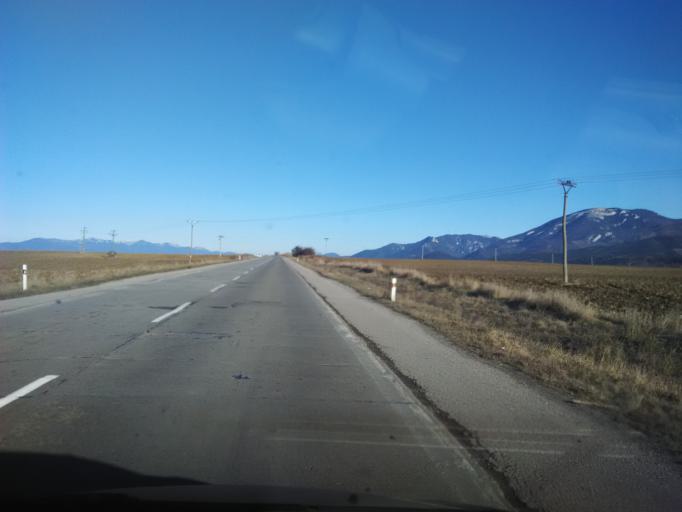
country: SK
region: Zilinsky
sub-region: Okres Martin
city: Martin
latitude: 48.9007
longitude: 18.8724
